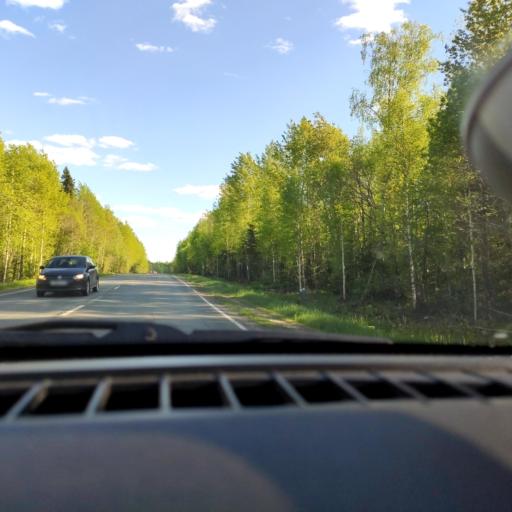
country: RU
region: Perm
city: Polazna
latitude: 58.2741
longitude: 56.1664
